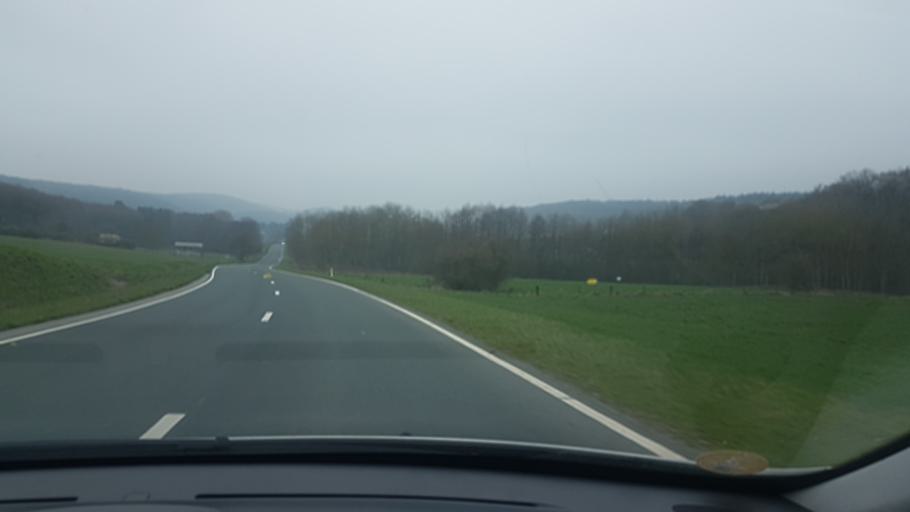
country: BE
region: Wallonia
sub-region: Province de Namur
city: Couvin
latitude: 50.0679
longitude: 4.5742
